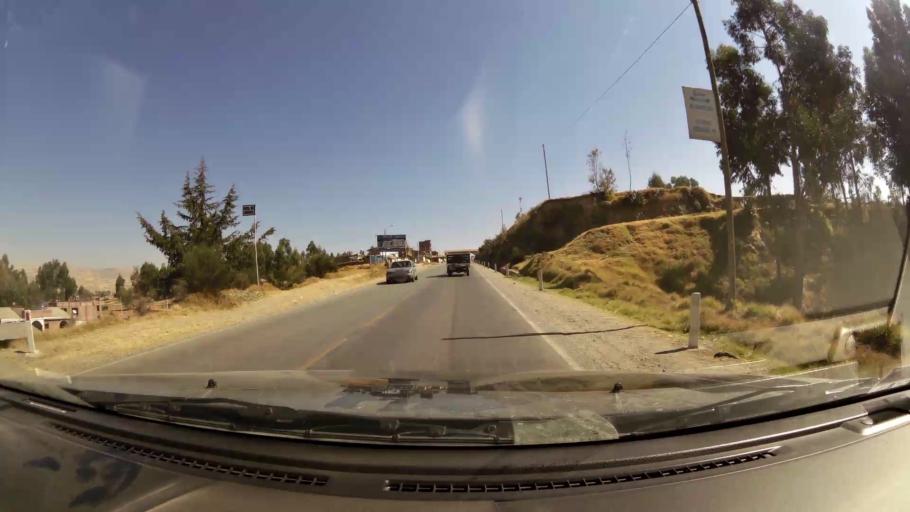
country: PE
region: Junin
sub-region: Provincia de Concepcion
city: Concepcion
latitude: -11.9252
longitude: -75.3167
